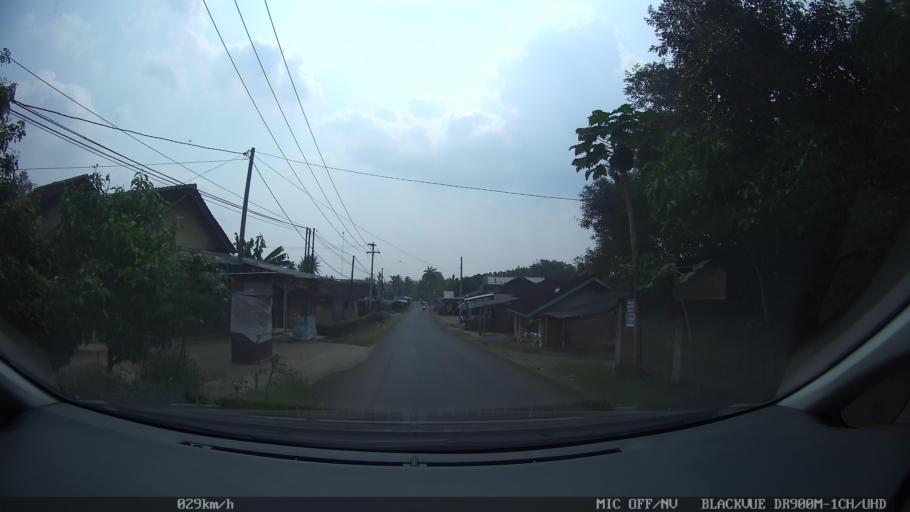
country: ID
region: Lampung
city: Gadingrejo
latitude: -5.3496
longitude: 105.0314
